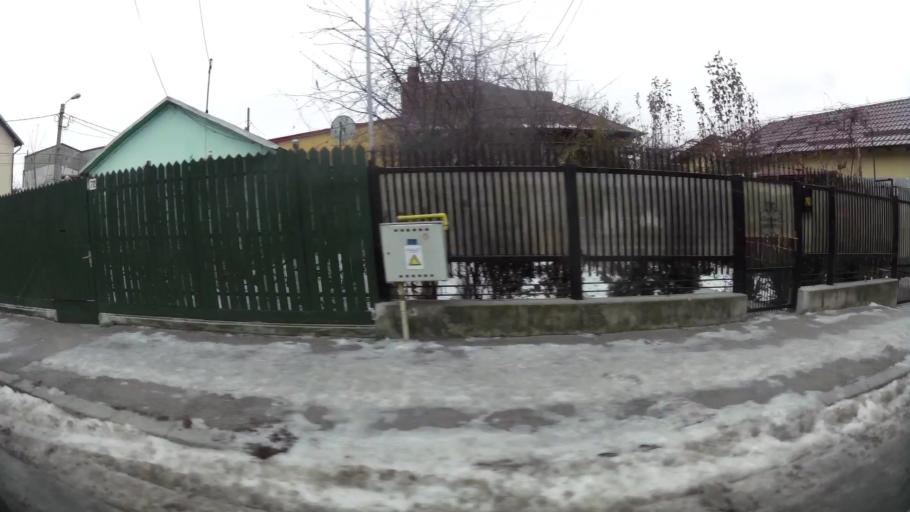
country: RO
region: Prahova
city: Ploiesti
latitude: 44.9434
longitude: 26.0450
